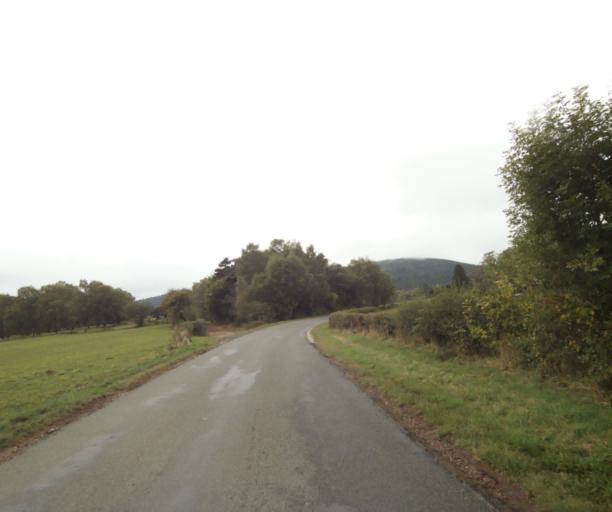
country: FR
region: Auvergne
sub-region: Departement du Puy-de-Dome
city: Saint-Genes-Champanelle
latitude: 45.7297
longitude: 2.9746
